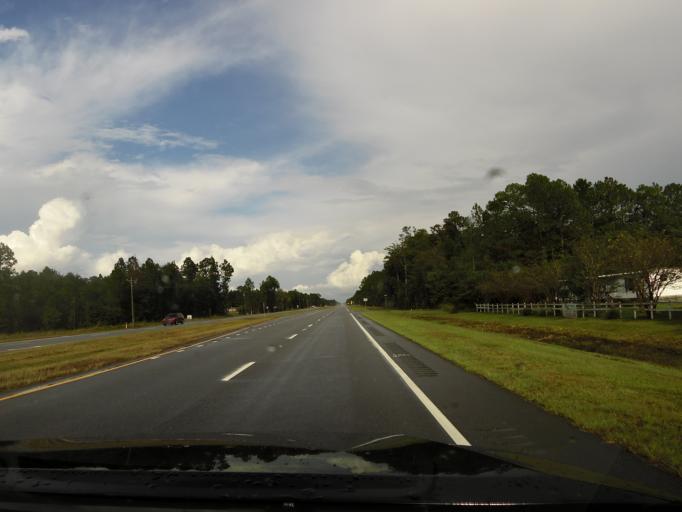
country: US
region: Georgia
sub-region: Long County
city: Ludowici
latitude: 31.7405
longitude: -81.6945
